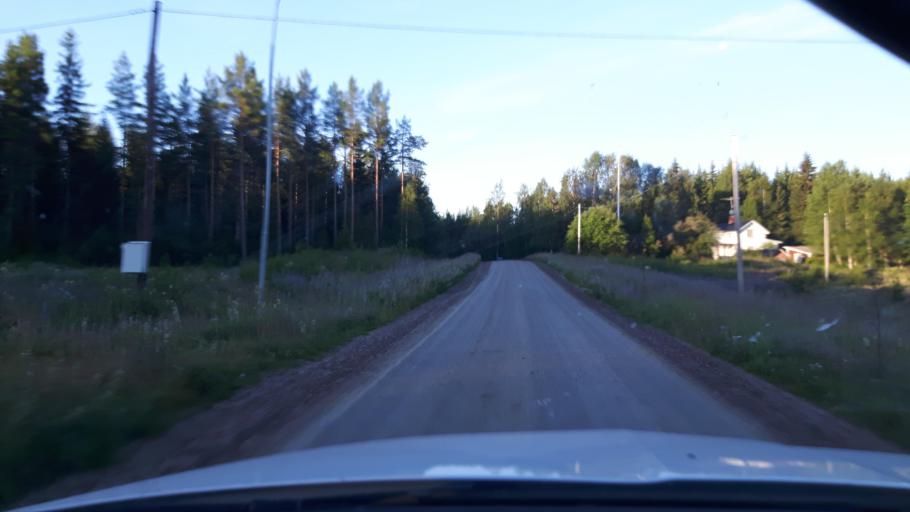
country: SE
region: Vaesternorrland
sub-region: Ange Kommun
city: Ange
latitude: 62.1467
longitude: 15.6612
